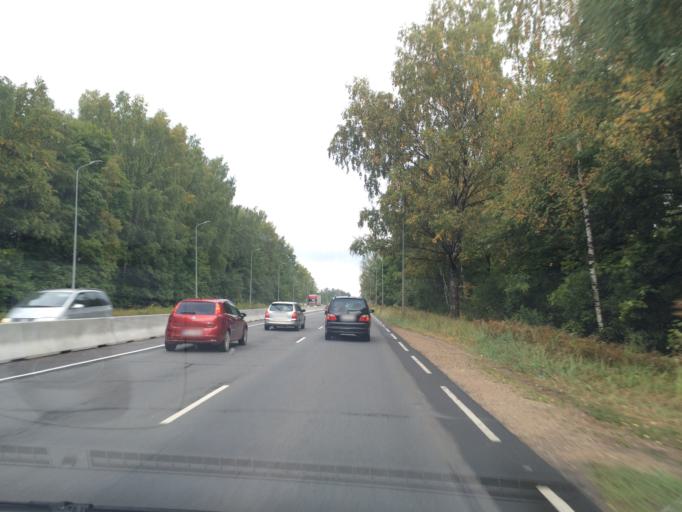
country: LV
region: Kekava
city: Kekava
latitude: 56.8744
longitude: 24.2645
